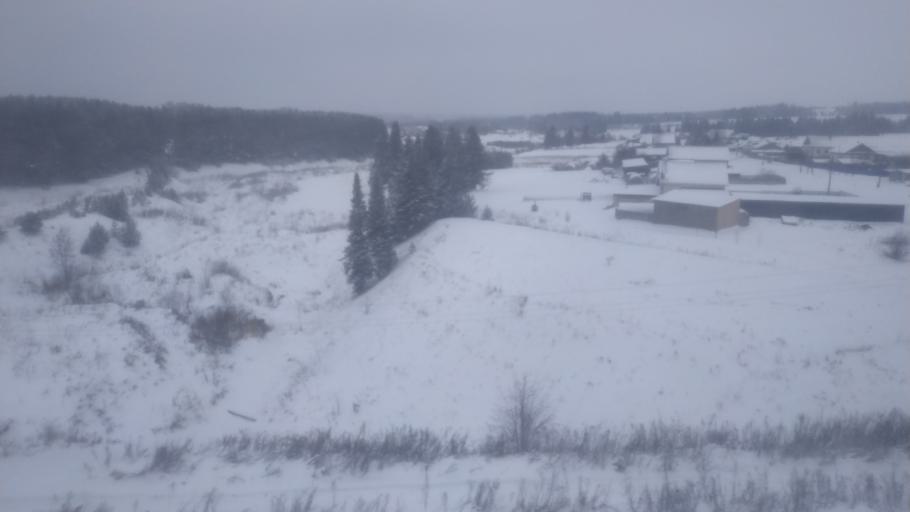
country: RU
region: Udmurtiya
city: Kiyasovo
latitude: 56.5025
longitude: 53.2208
